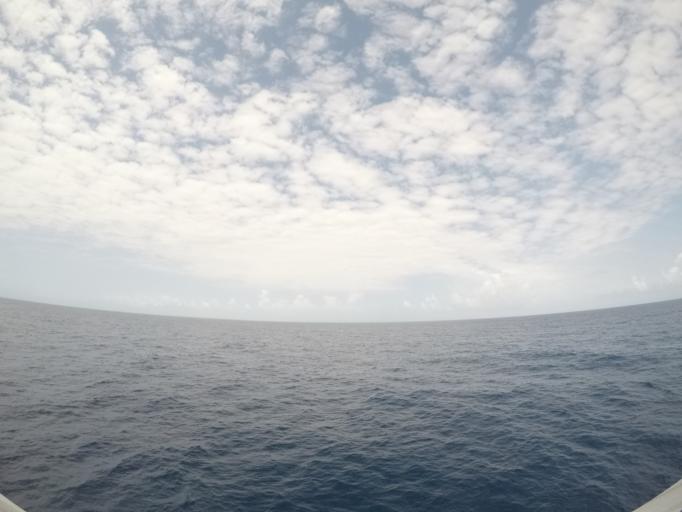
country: TZ
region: Zanzibar North
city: Nungwi
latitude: -5.5878
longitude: 39.3520
